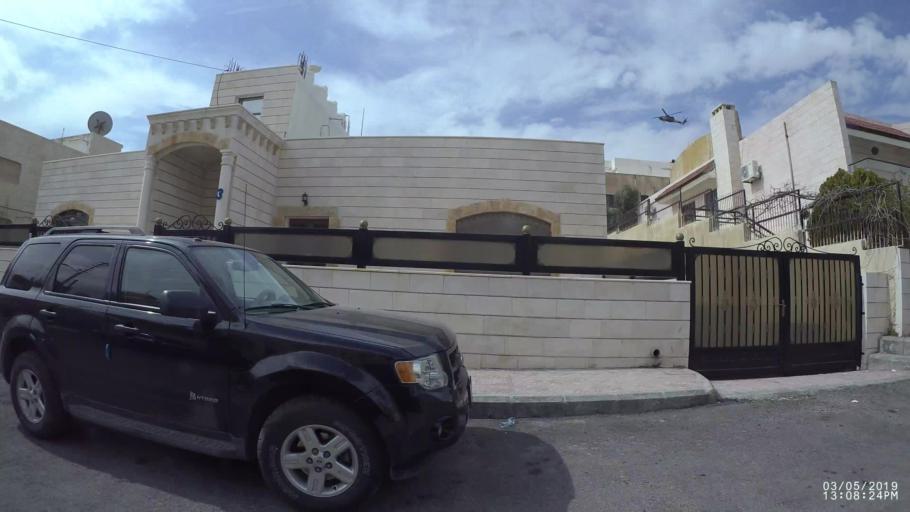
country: JO
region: Amman
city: Amman
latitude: 31.9977
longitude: 35.9371
